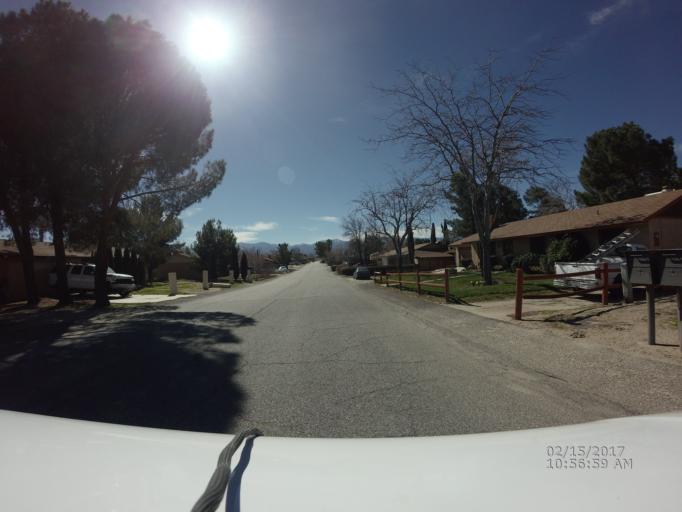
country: US
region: California
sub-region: Los Angeles County
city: Lake Los Angeles
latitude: 34.5845
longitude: -117.8517
